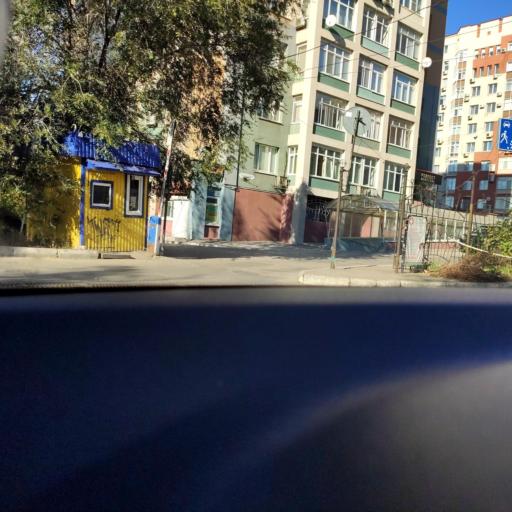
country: RU
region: Samara
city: Samara
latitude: 53.2094
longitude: 50.1232
